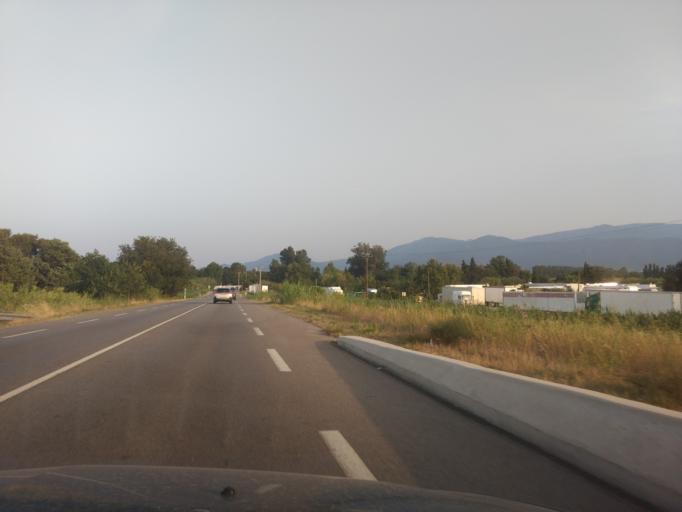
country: FR
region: Languedoc-Roussillon
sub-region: Departement des Pyrenees-Orientales
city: Latour-Bas-Elne
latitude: 42.5847
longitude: 3.0309
